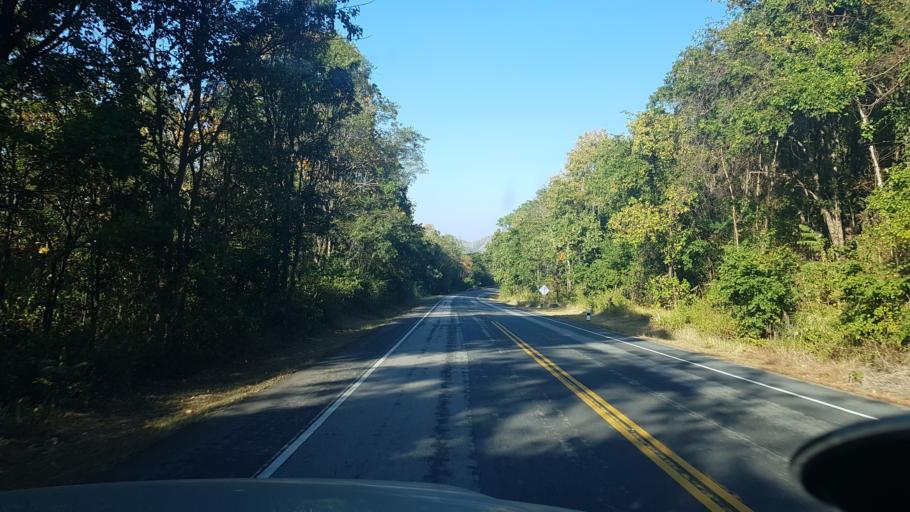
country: TH
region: Phetchabun
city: Lom Sak
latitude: 16.7394
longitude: 101.4169
